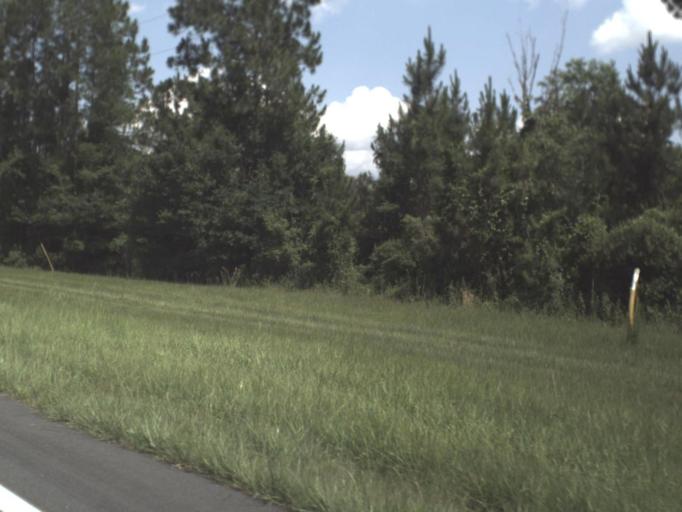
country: US
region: Florida
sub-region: Bradford County
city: Starke
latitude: 29.9386
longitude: -82.0678
